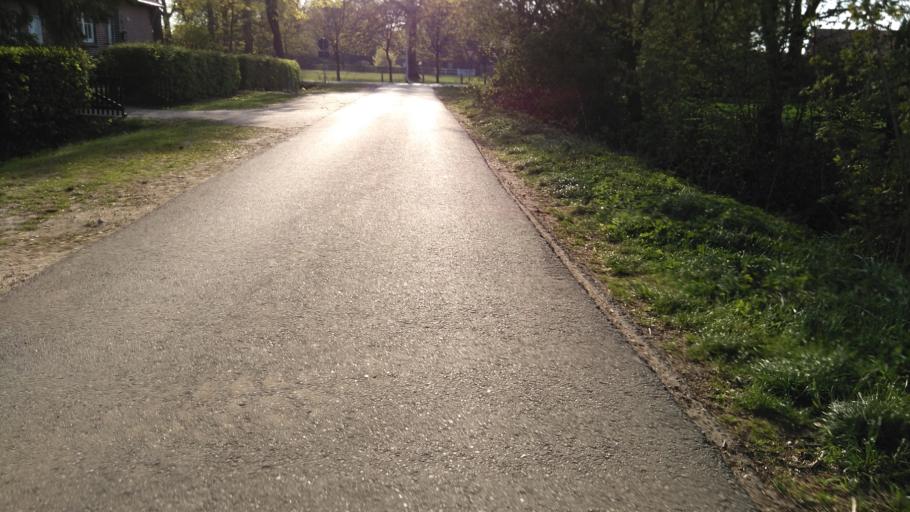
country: DE
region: Lower Saxony
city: Apensen
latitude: 53.4327
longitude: 9.6245
